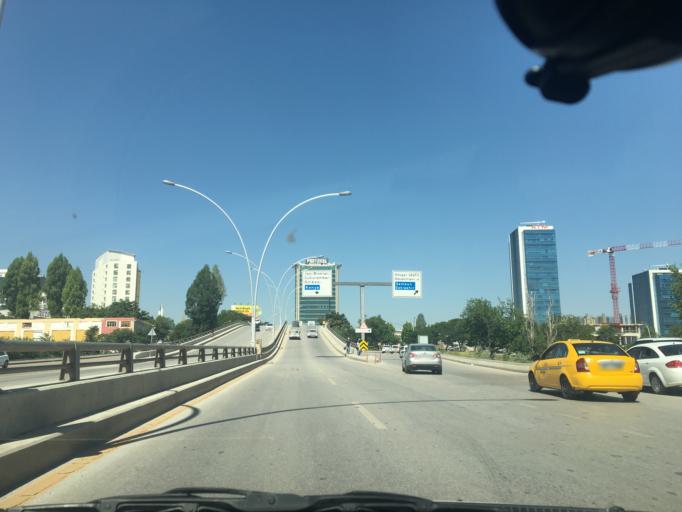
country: TR
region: Ankara
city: Ankara
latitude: 39.8974
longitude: 32.8163
